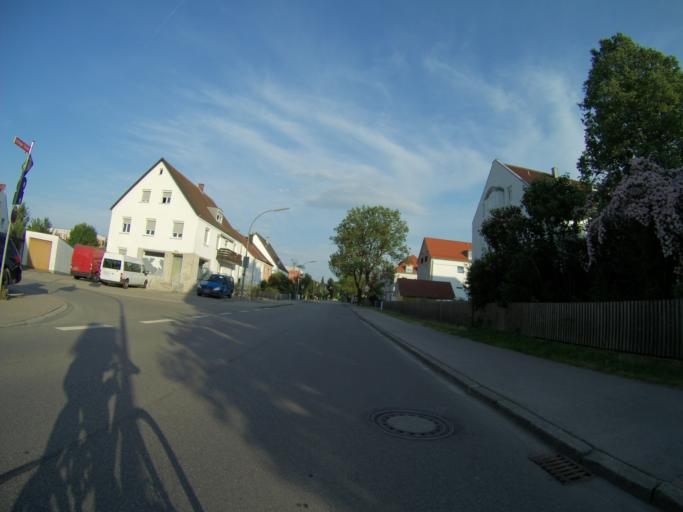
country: DE
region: Bavaria
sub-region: Upper Bavaria
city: Freising
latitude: 48.3920
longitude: 11.7616
